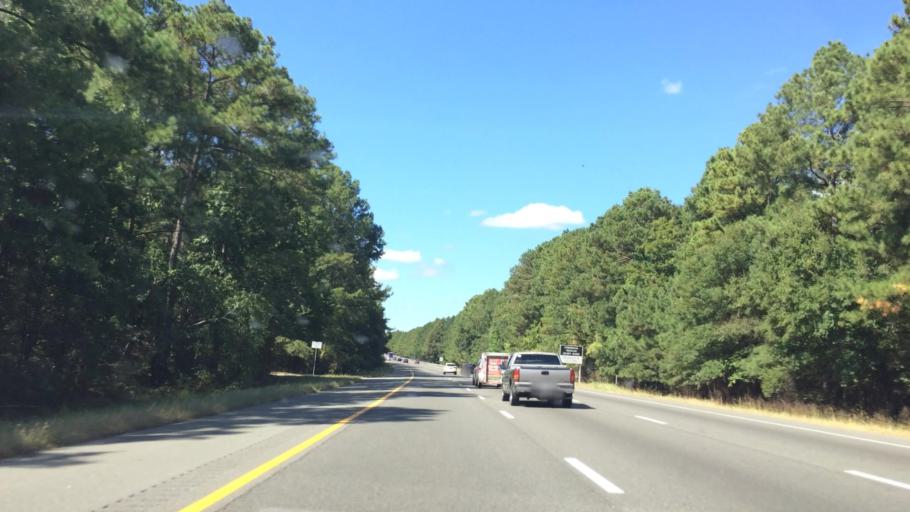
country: US
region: Virginia
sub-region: Henrico County
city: Glen Allen
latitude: 37.6732
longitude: -77.4942
